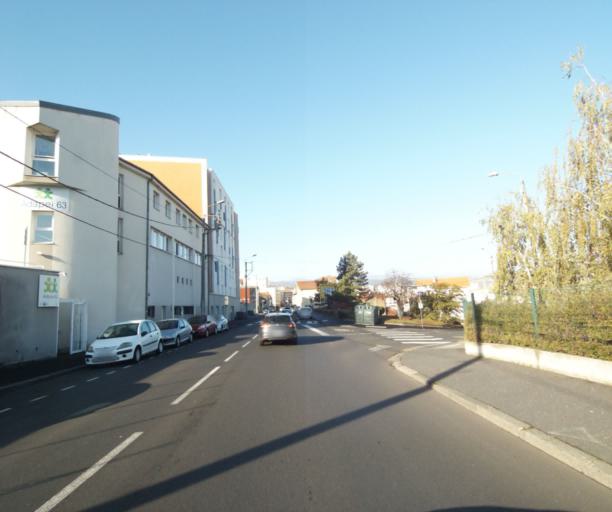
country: FR
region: Auvergne
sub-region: Departement du Puy-de-Dome
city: Aubiere
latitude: 45.7702
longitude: 3.1066
